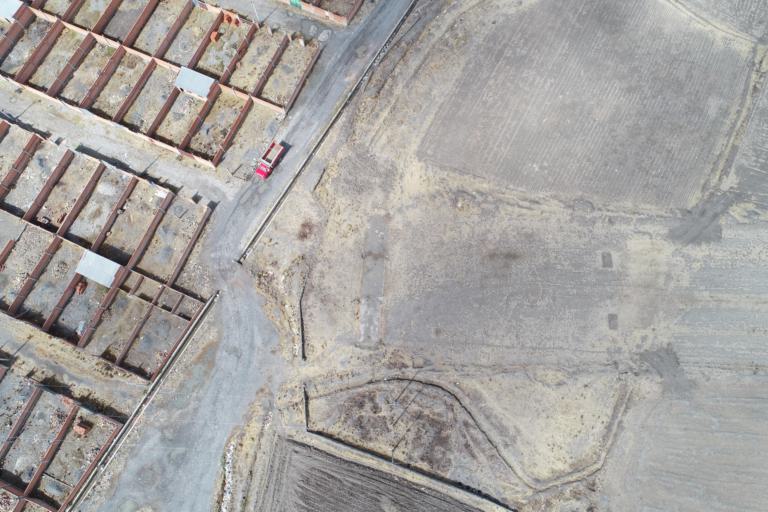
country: BO
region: La Paz
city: Achacachi
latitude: -16.0368
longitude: -68.6845
